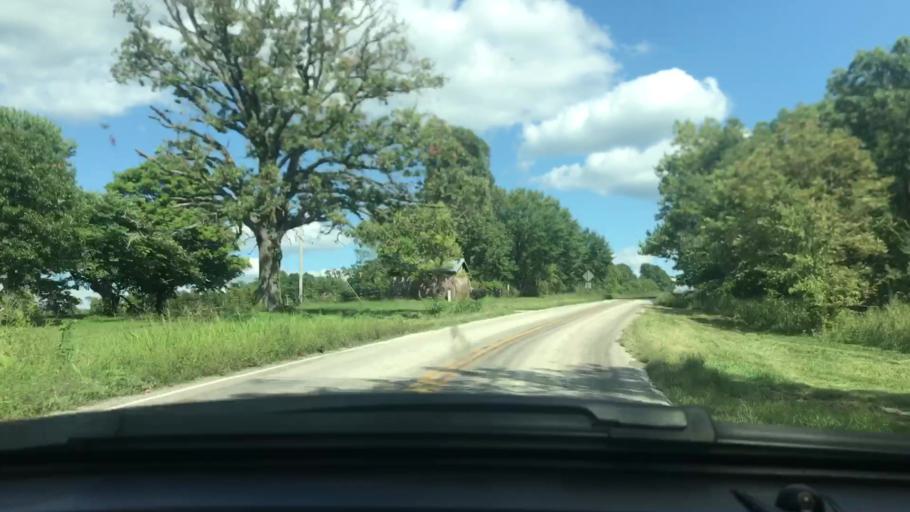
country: US
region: Missouri
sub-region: Wright County
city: Hartville
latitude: 37.3767
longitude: -92.3803
